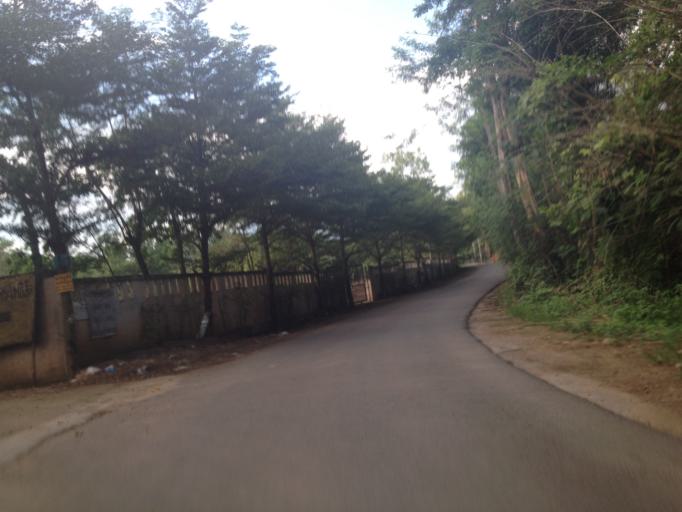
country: TH
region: Chiang Mai
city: Hang Dong
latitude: 18.7171
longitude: 98.9049
